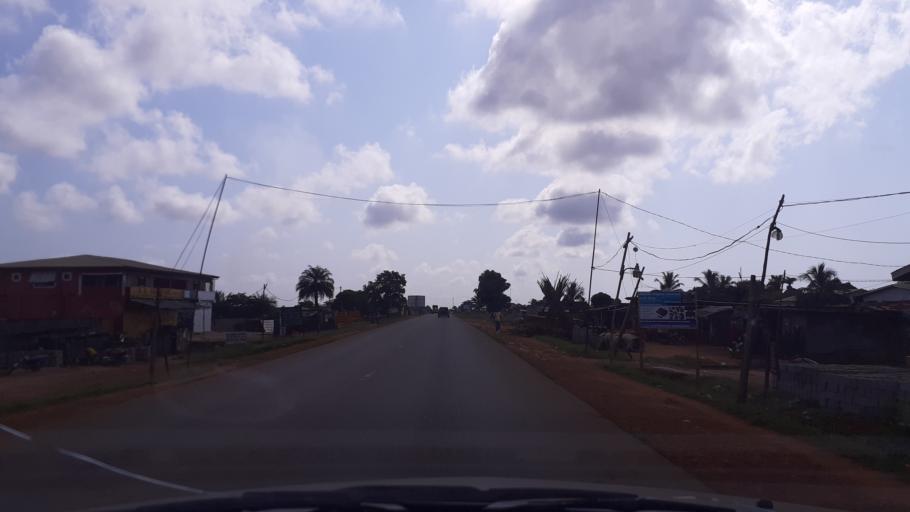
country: LR
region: Montserrado
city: Monrovia
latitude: 6.2226
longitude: -10.6021
